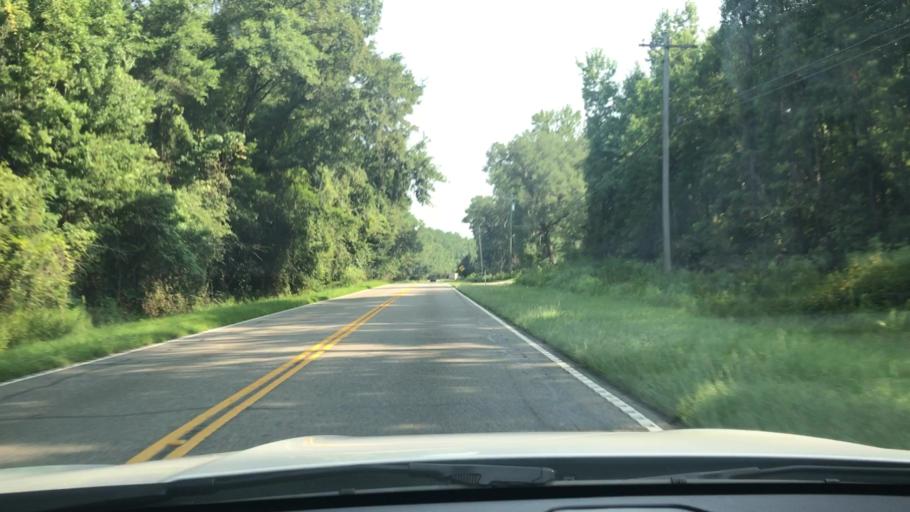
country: US
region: South Carolina
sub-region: Georgetown County
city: Georgetown
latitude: 33.4720
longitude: -79.2791
